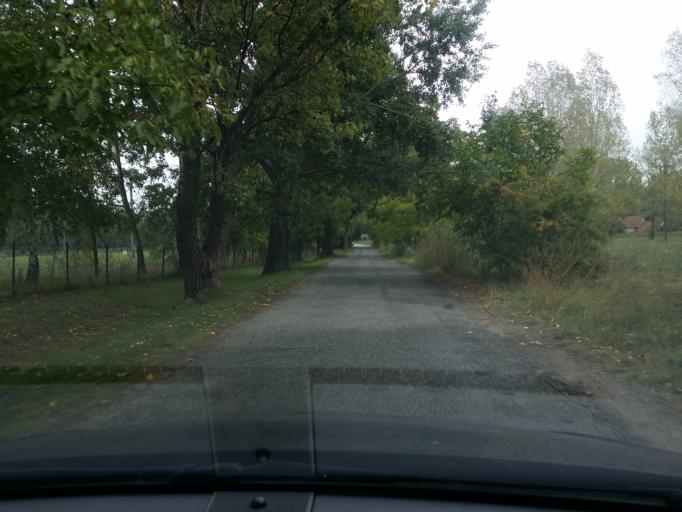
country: HU
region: Pest
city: Szigetcsep
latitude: 47.2311
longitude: 18.9644
